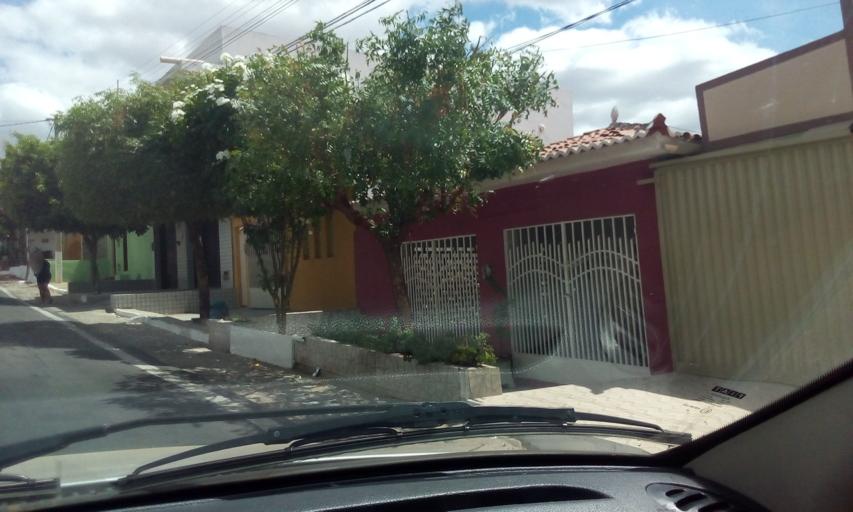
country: BR
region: Rio Grande do Norte
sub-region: Currais Novos
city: Currais Novos
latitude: -6.2647
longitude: -36.5192
